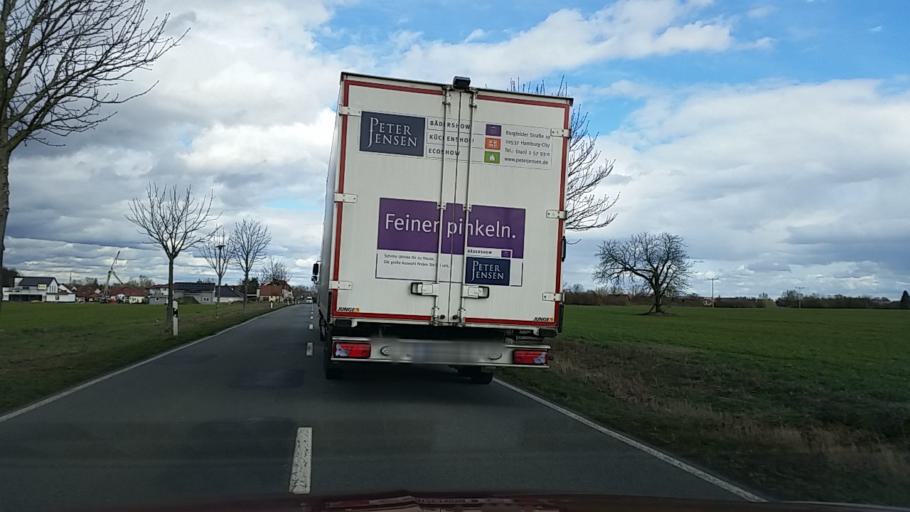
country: DE
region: Saxony-Anhalt
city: Salzwedel
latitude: 52.8357
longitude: 11.1470
